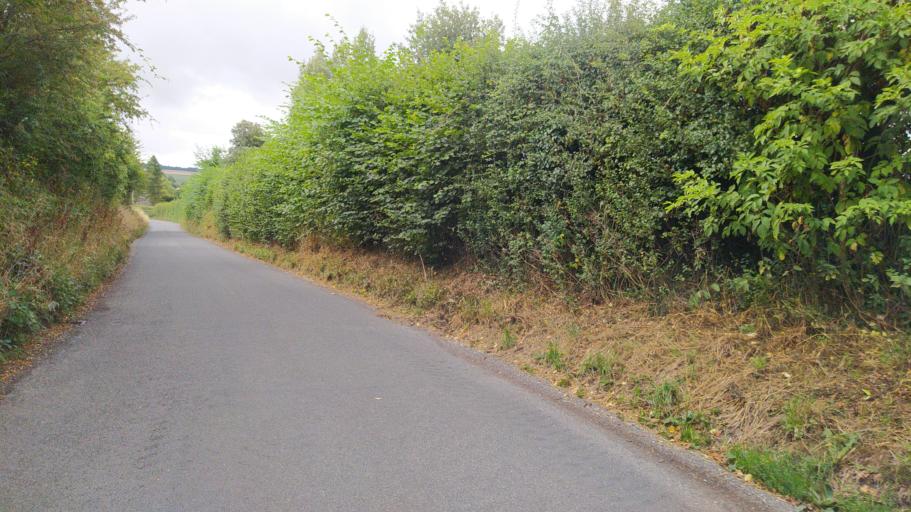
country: GB
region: England
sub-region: Hampshire
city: Petersfield
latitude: 50.9870
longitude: -1.0154
